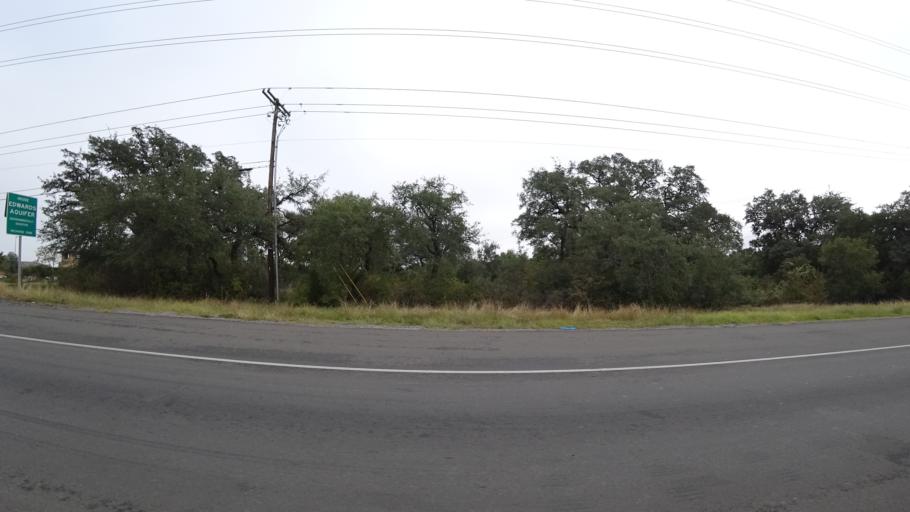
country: US
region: Texas
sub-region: Travis County
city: Shady Hollow
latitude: 30.1996
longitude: -97.8660
